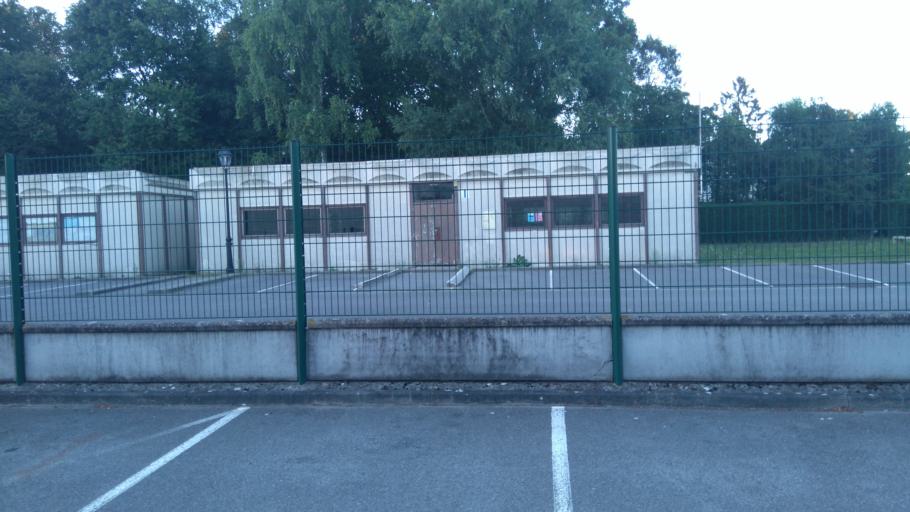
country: FR
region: Picardie
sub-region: Departement de l'Oise
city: Saint-Maximin
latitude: 49.2339
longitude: 2.4584
